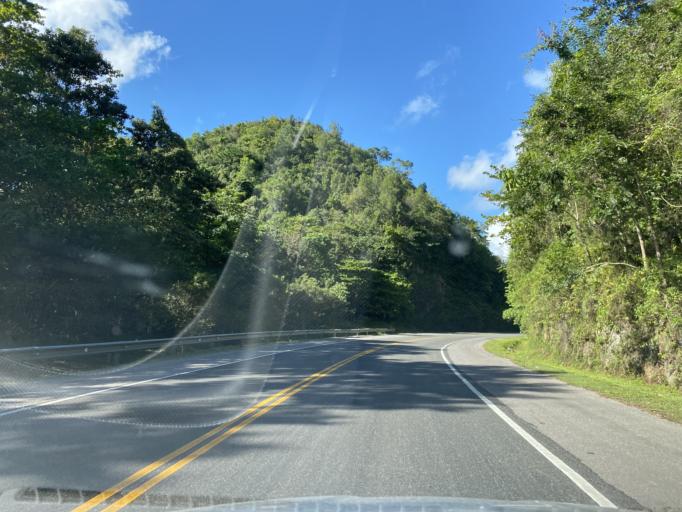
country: DO
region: Monte Plata
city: Majagual
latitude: 19.0623
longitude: -69.8284
